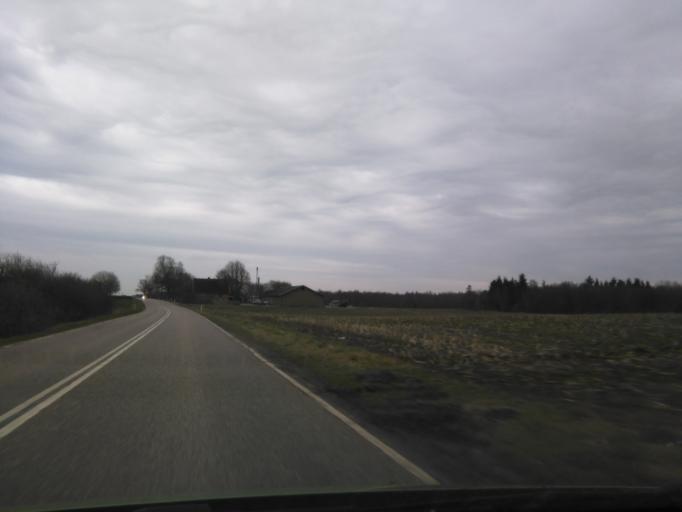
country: DK
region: Central Jutland
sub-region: Randers Kommune
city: Spentrup
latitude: 56.5655
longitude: 9.9990
